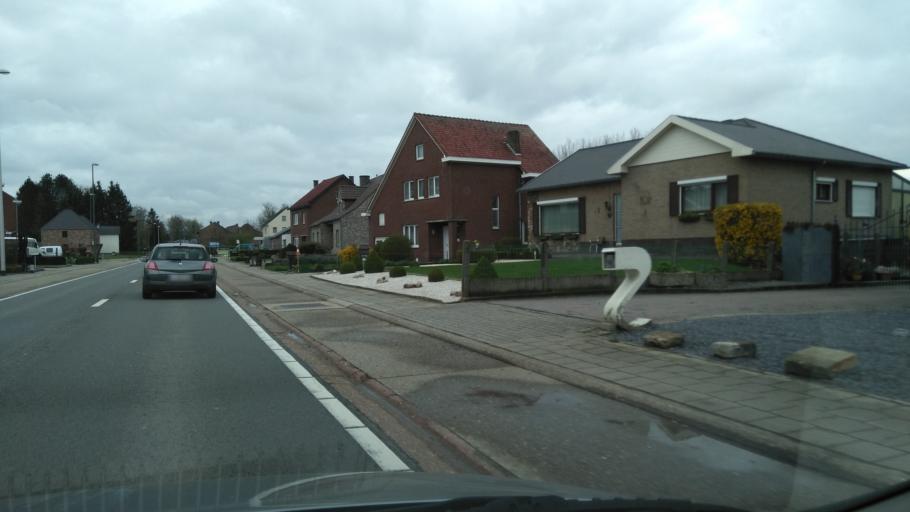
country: BE
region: Flanders
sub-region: Provincie Limburg
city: Bilzen
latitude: 50.8479
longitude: 5.5405
